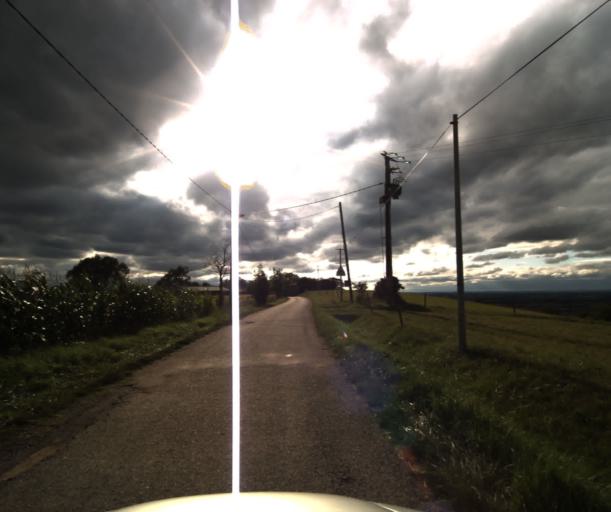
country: FR
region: Midi-Pyrenees
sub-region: Departement de la Haute-Garonne
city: Le Fauga
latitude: 43.3993
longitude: 1.3184
